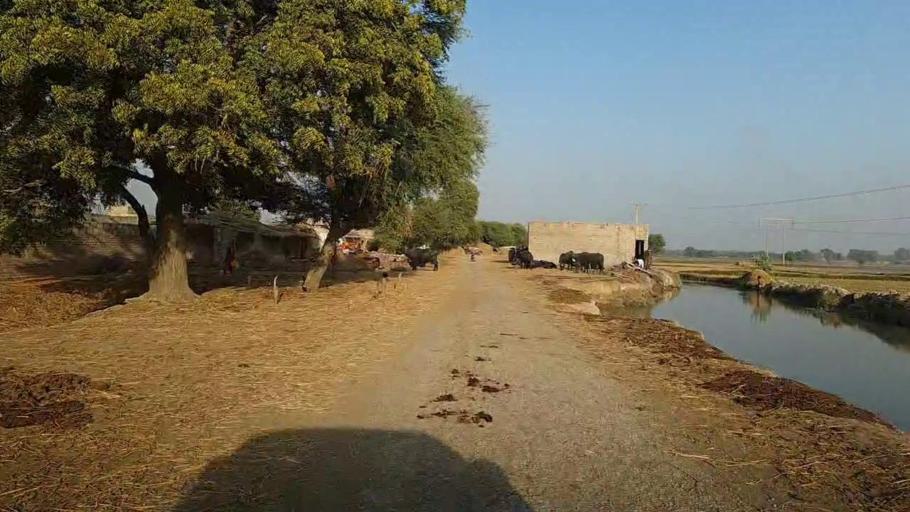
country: PK
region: Sindh
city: Kashmor
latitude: 28.4273
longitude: 69.4493
